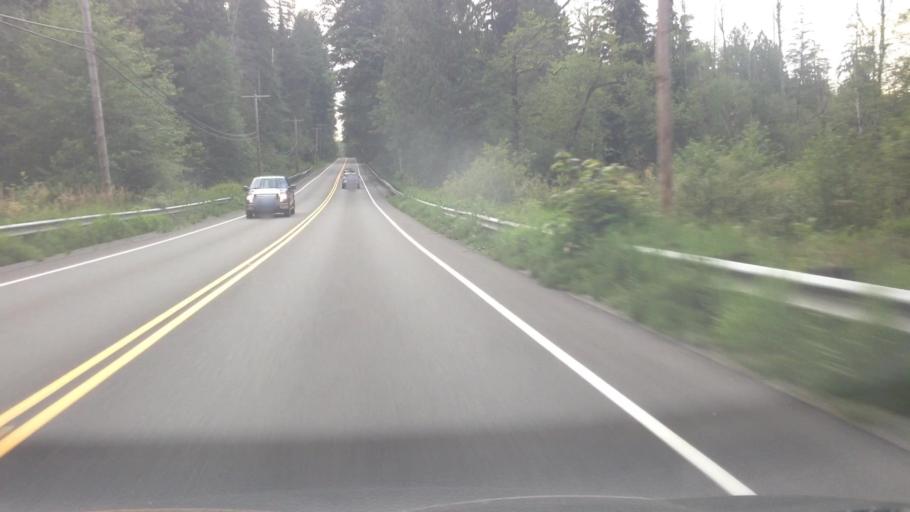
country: US
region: Washington
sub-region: King County
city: Duvall
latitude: 47.7569
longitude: -122.0262
